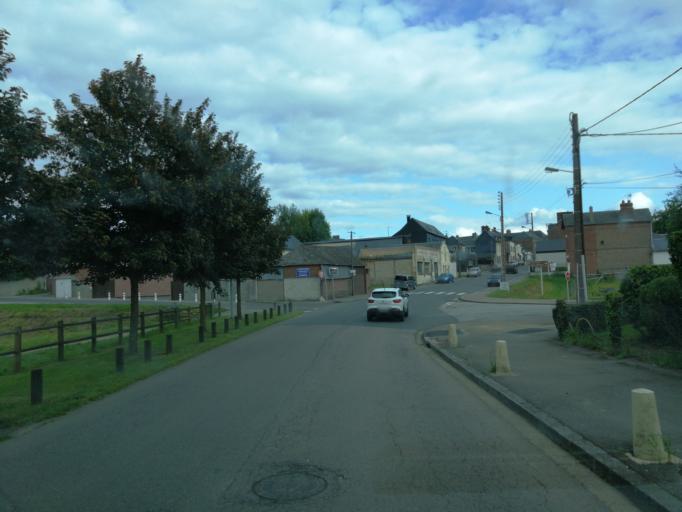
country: FR
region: Haute-Normandie
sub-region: Departement de l'Eure
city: Le Neubourg
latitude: 49.1502
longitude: 0.8989
